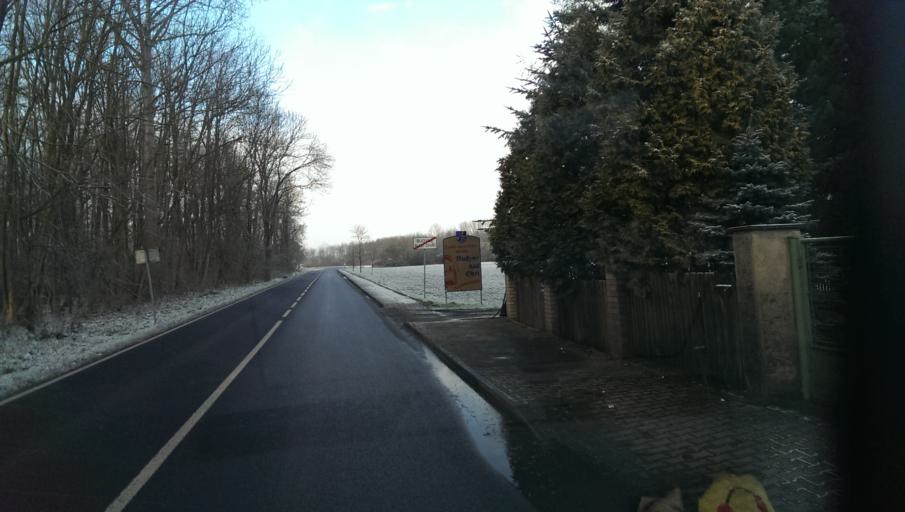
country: CZ
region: Ustecky
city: Budyne nad Ohri
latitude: 50.4071
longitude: 14.1232
